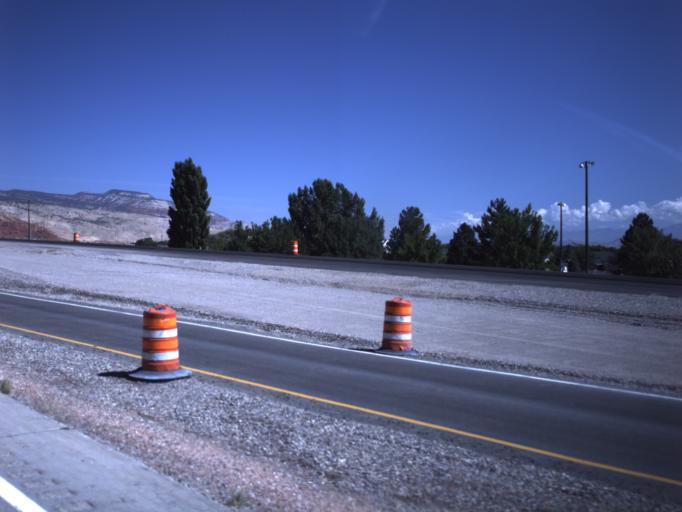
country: US
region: Utah
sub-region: Sevier County
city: Richfield
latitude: 38.7578
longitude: -112.1054
